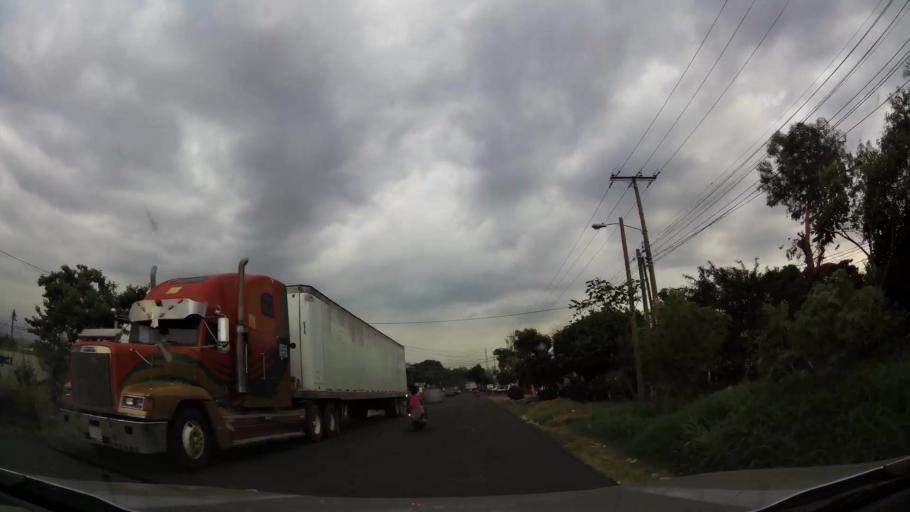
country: GT
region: Escuintla
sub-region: Municipio de Escuintla
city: Escuintla
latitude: 14.2910
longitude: -90.7810
